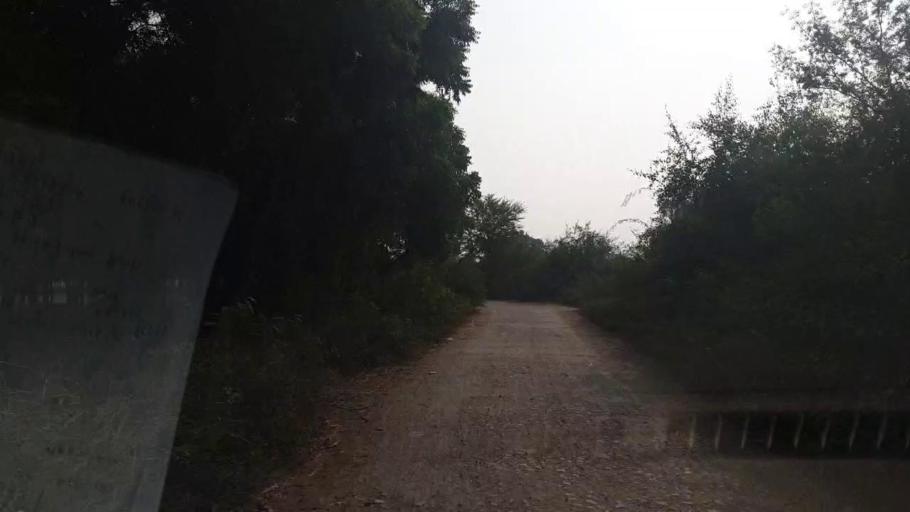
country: PK
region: Sindh
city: Tando Jam
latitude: 25.3373
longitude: 68.5203
